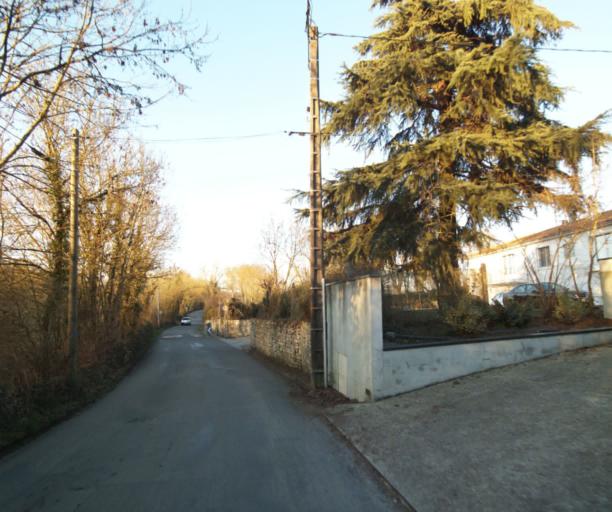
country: FR
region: Poitou-Charentes
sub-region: Departement des Deux-Sevres
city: Niort
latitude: 46.3580
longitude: -0.4525
